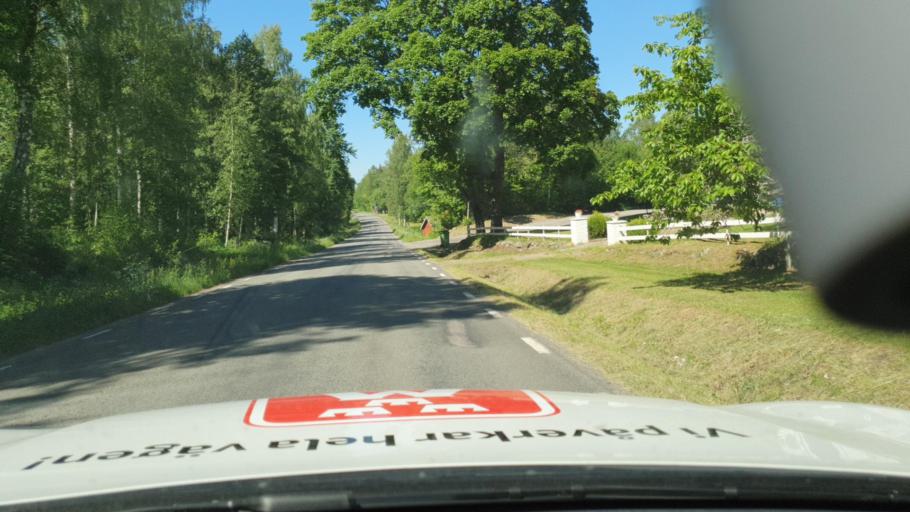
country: SE
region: Vaestra Goetaland
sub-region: Tidaholms Kommun
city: Tidaholm
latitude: 58.1190
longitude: 14.0663
